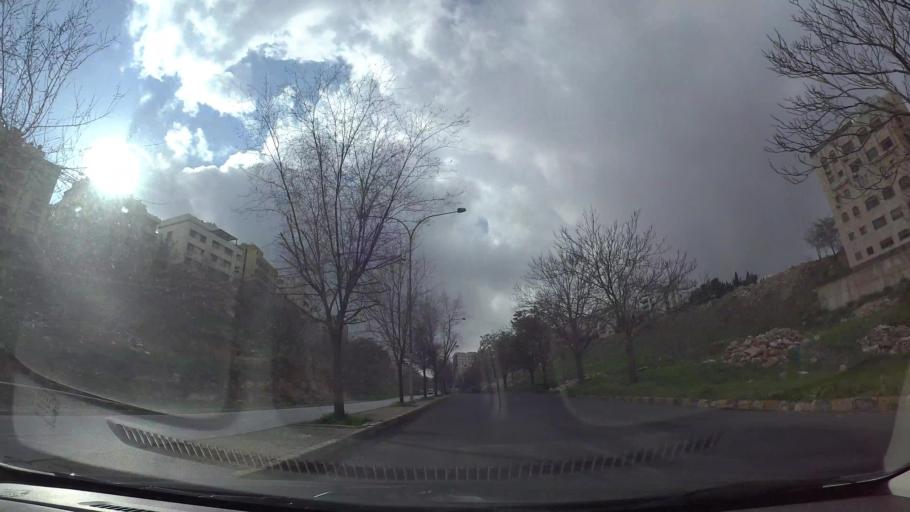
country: JO
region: Amman
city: Amman
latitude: 31.9413
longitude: 35.8988
